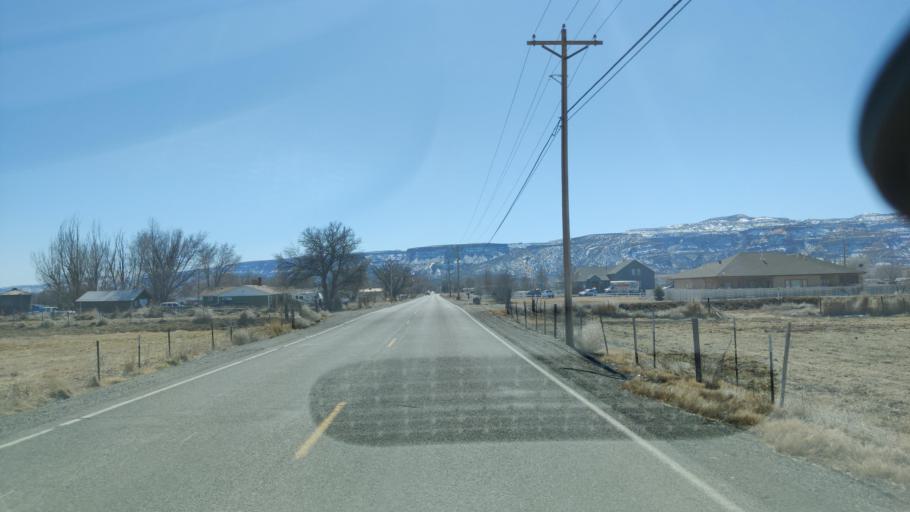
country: US
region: Colorado
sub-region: Mesa County
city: Fruita
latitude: 39.1467
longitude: -108.7011
